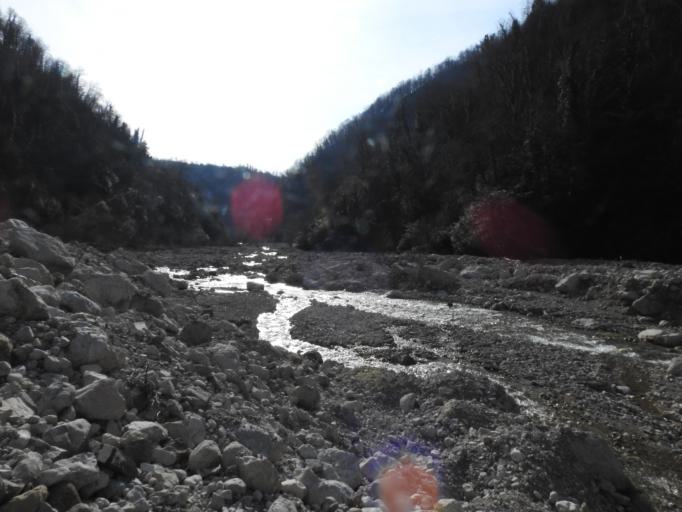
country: GE
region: Abkhazia
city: Gudauta
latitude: 43.2467
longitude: 40.6609
